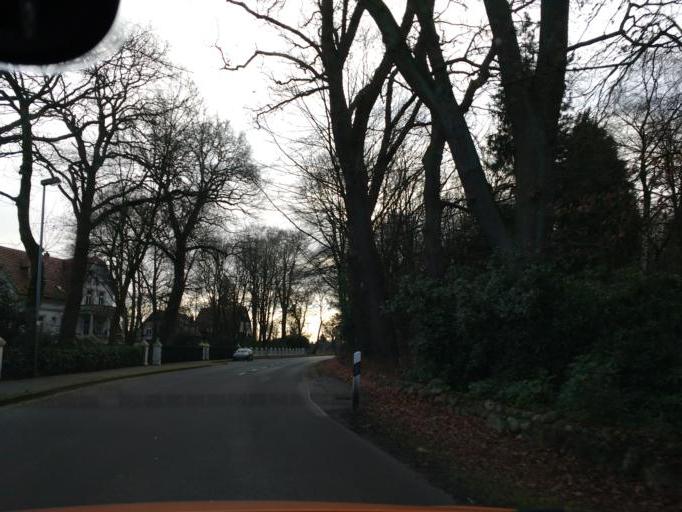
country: DE
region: Lower Saxony
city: Hude
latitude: 53.1070
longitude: 8.4520
